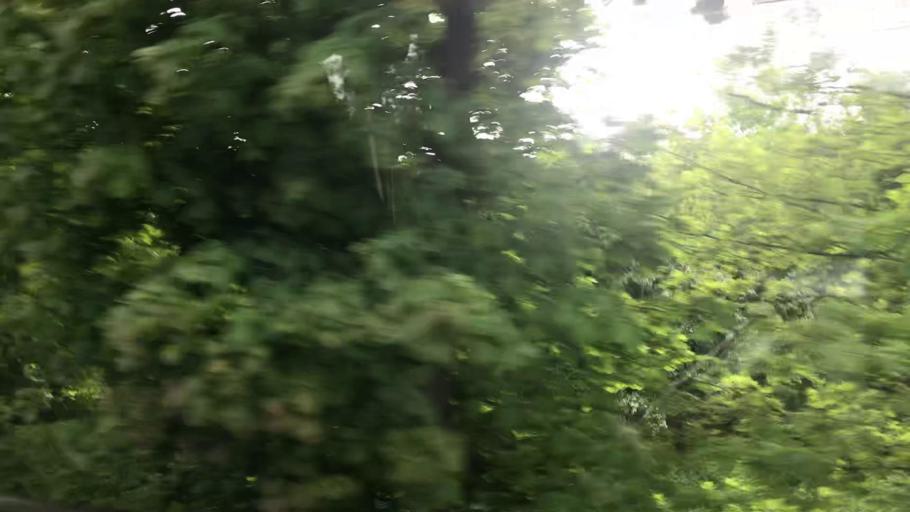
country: PL
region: Lower Silesian Voivodeship
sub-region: Powiat walbrzyski
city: Walbrzych
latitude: 50.7671
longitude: 16.2518
